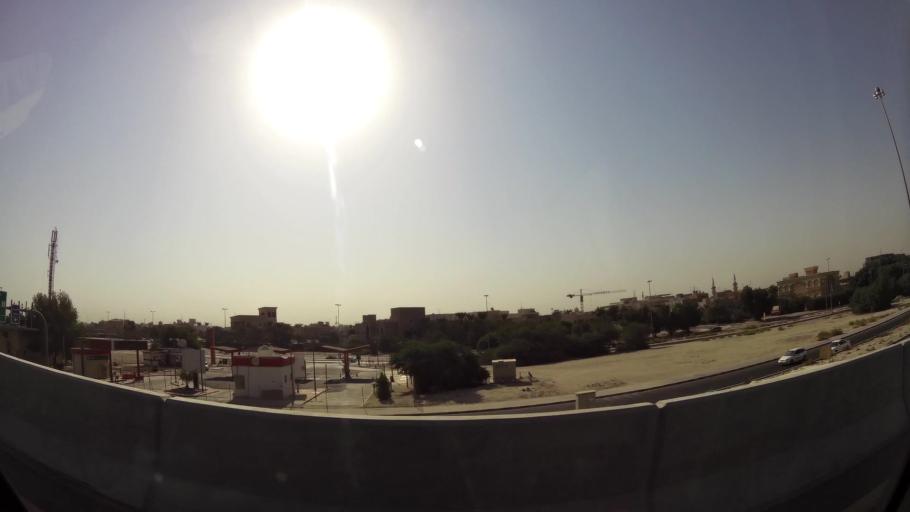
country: KW
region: Al Asimah
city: Ash Shamiyah
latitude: 29.3598
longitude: 47.9581
